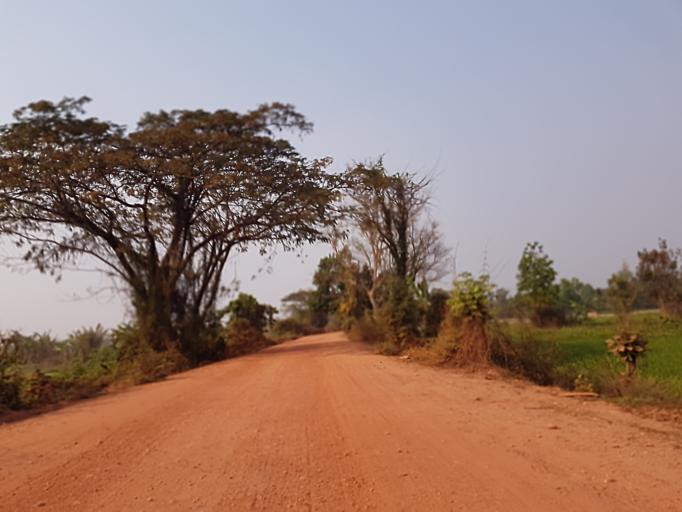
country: TH
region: Nong Khai
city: Phon Phisai
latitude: 18.0032
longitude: 102.9079
